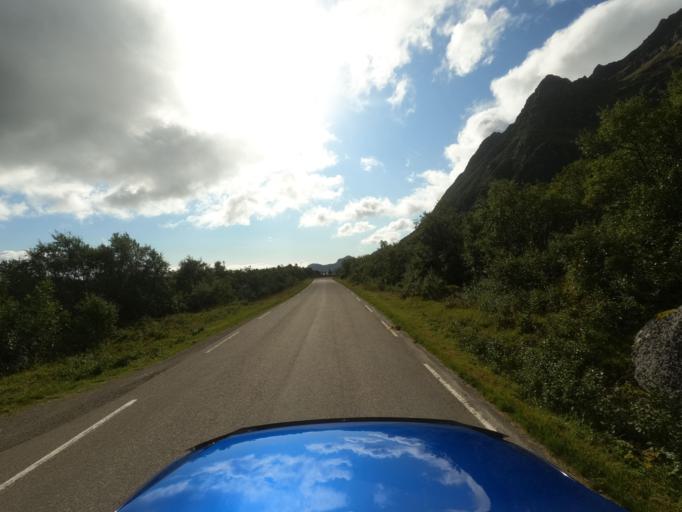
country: NO
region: Nordland
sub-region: Vestvagoy
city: Evjen
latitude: 68.1815
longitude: 13.8525
